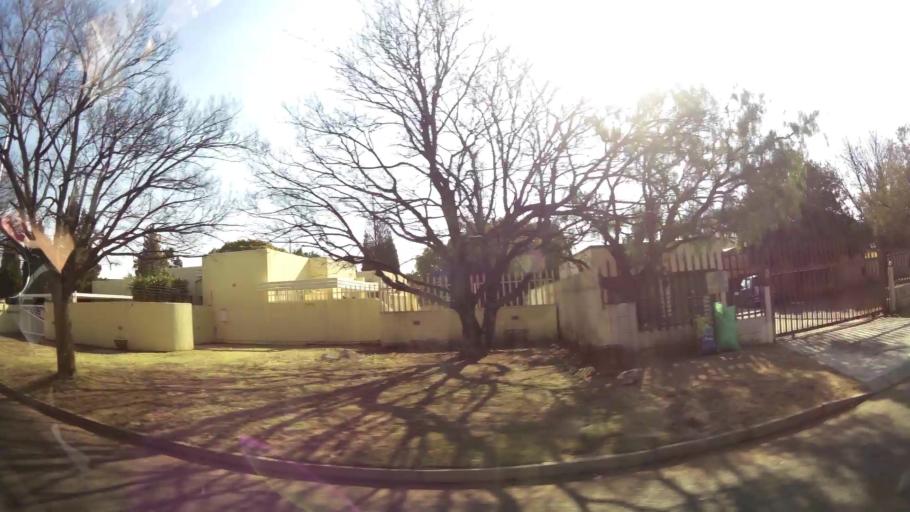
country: ZA
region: Gauteng
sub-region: West Rand District Municipality
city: Randfontein
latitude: -26.1522
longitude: 27.7047
